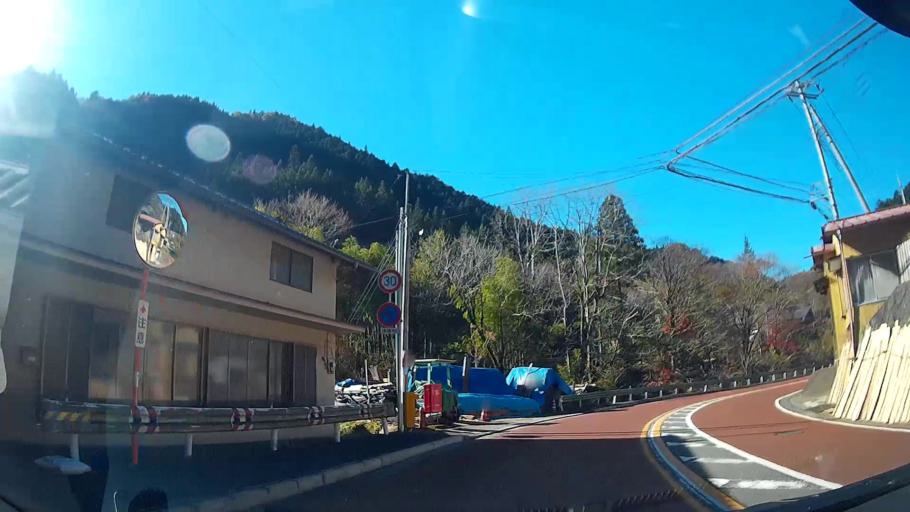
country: JP
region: Yamanashi
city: Uenohara
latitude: 35.7045
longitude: 139.1231
